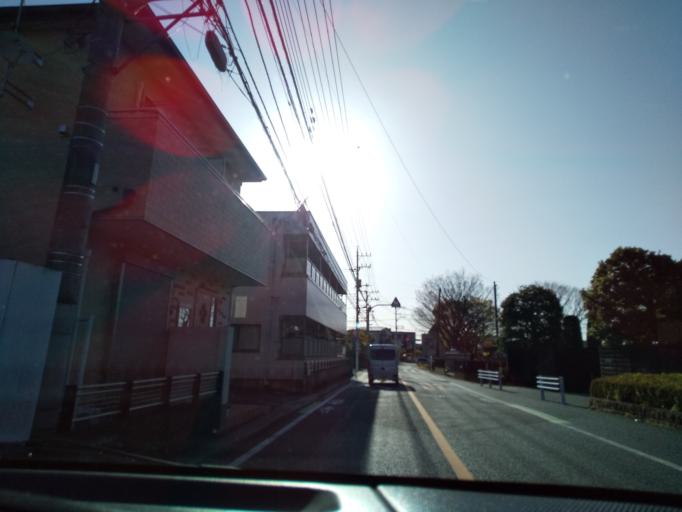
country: JP
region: Tokyo
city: Hino
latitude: 35.6964
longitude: 139.3967
